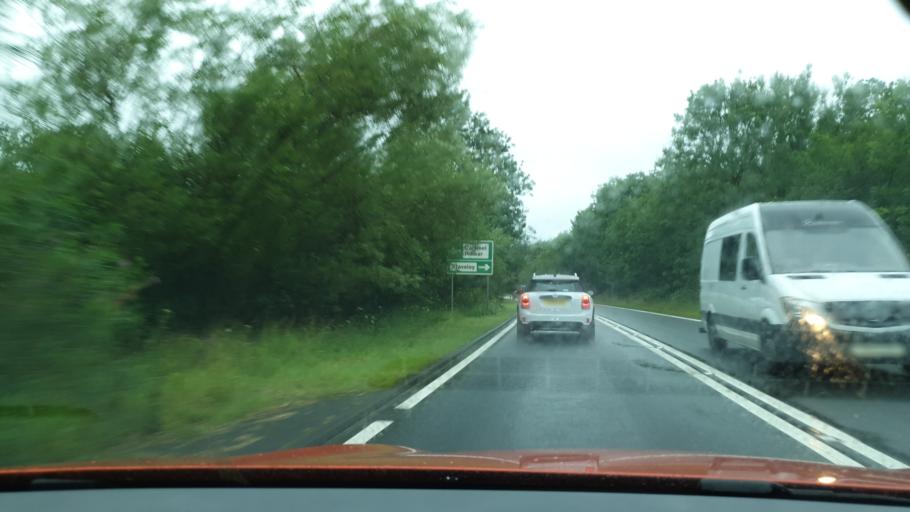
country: GB
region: England
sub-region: Cumbria
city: Grange-over-Sands
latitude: 54.2557
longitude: -2.9457
